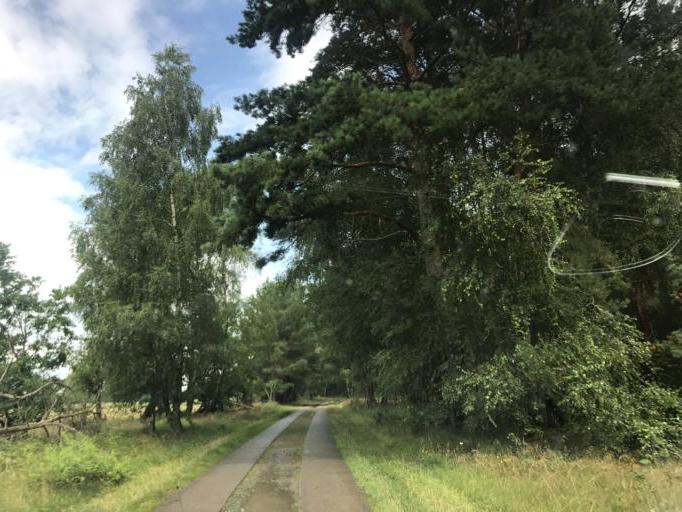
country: DE
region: Mecklenburg-Vorpommern
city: Wesenberg
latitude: 53.3761
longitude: 12.8941
